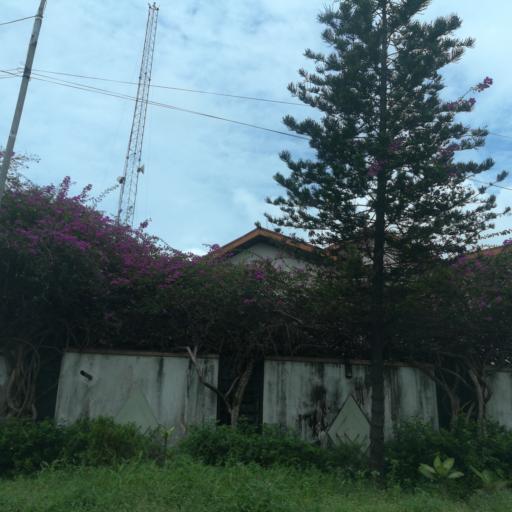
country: NG
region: Lagos
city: Ikoyi
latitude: 6.4439
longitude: 3.4597
